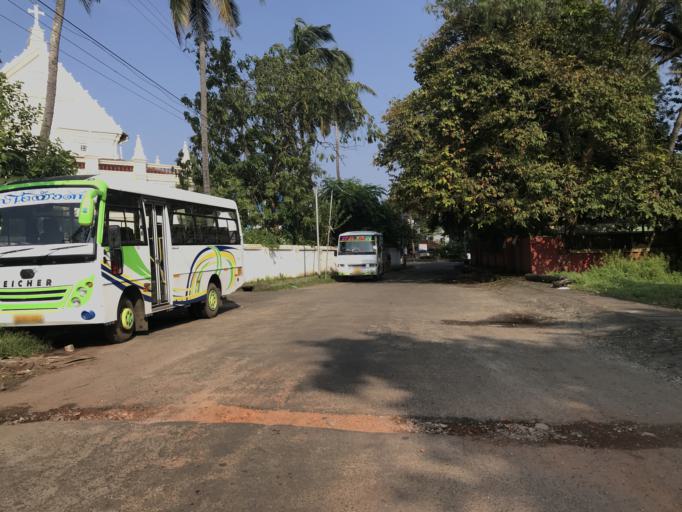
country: IN
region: Kerala
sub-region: Ernakulam
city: Cochin
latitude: 9.9645
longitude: 76.2423
